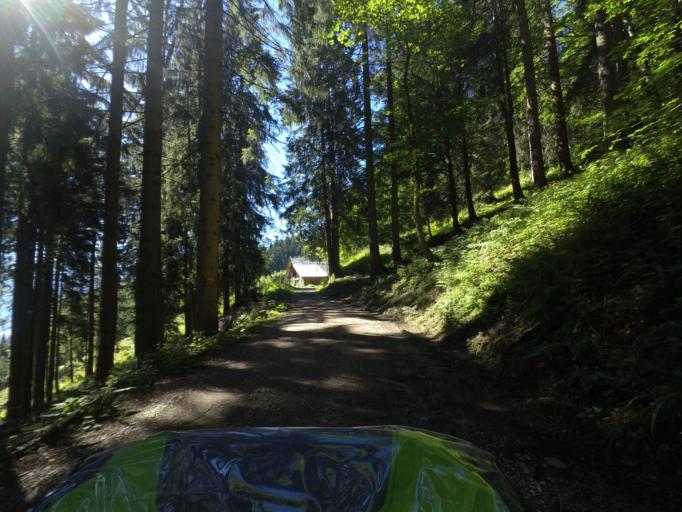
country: AT
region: Salzburg
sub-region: Politischer Bezirk Hallein
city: Kuchl
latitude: 47.6352
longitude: 13.1033
